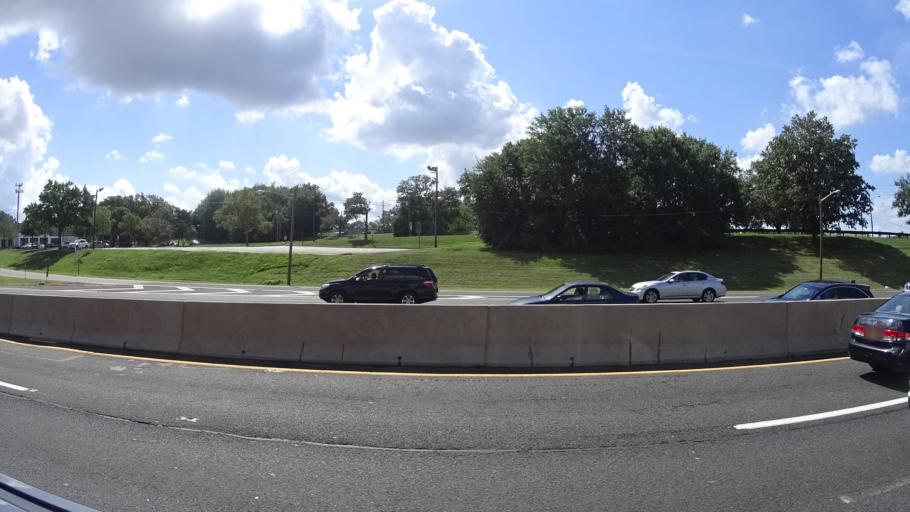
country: US
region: New Jersey
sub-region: Union County
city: Union
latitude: 40.6989
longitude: -74.2538
